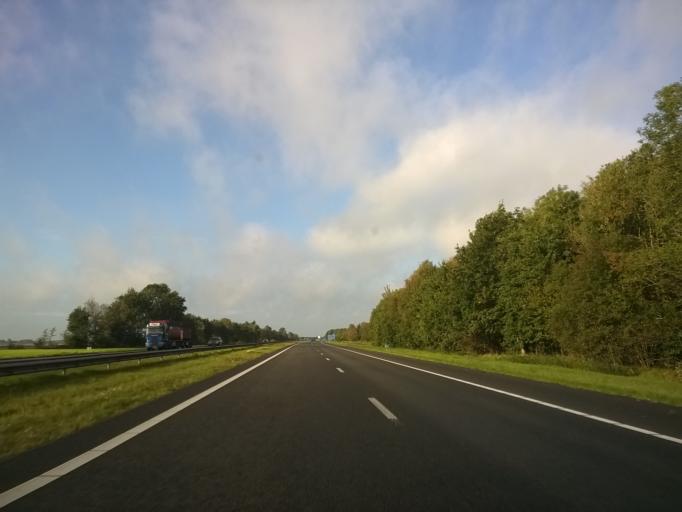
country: NL
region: Friesland
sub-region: Gemeente Achtkarspelen
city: Surhuisterveen
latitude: 53.1387
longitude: 6.2159
